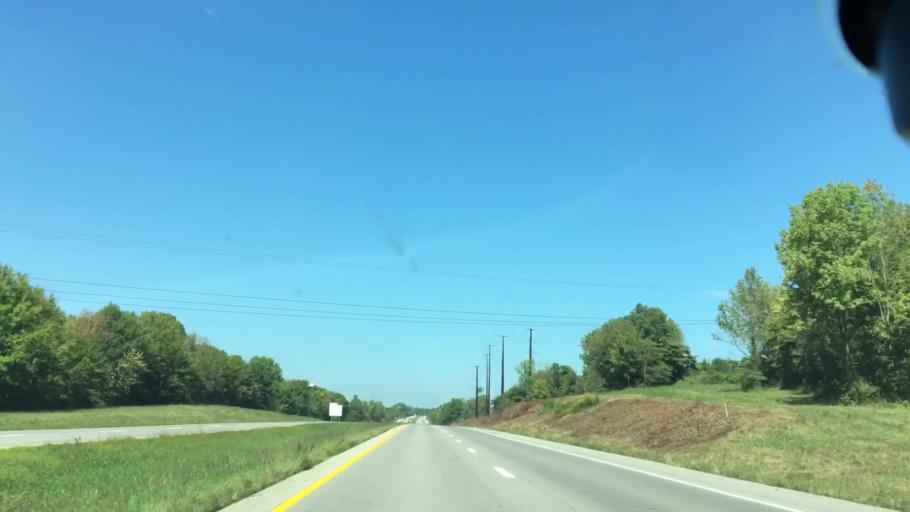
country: US
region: Kentucky
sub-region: Webster County
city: Sebree
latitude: 37.6382
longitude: -87.5100
